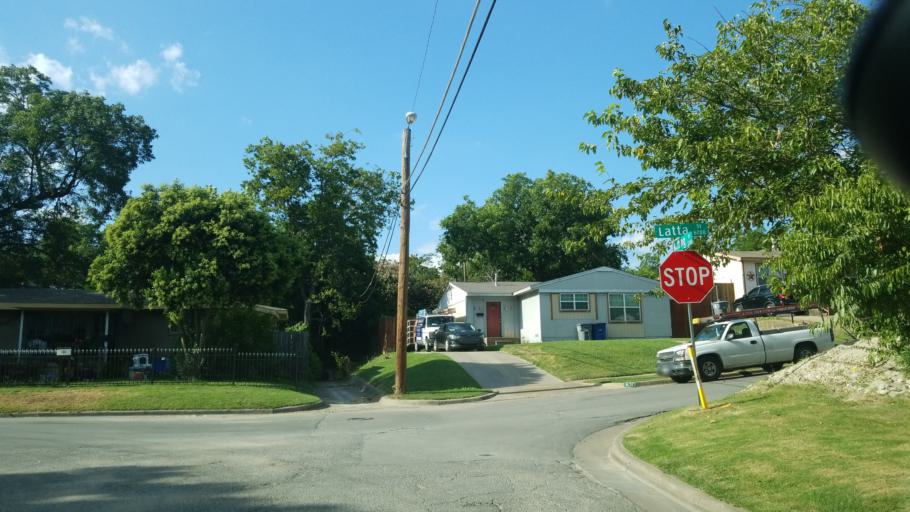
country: US
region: Texas
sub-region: Dallas County
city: Balch Springs
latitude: 32.7662
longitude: -96.7056
